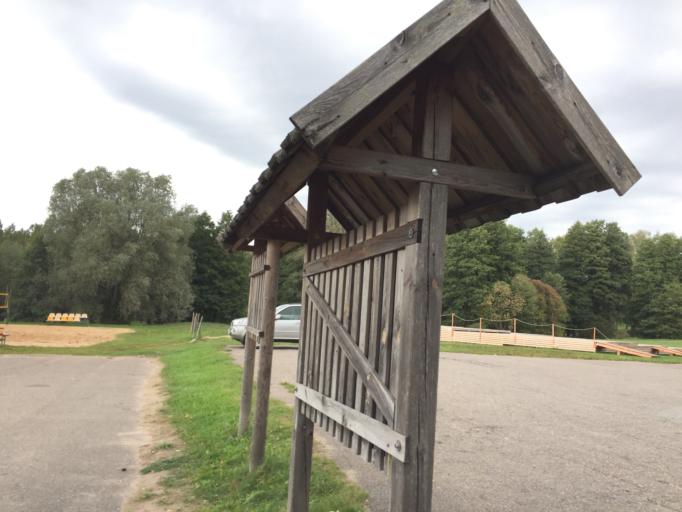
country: LV
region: Limbazu Rajons
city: Limbazi
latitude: 57.5028
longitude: 24.7054
